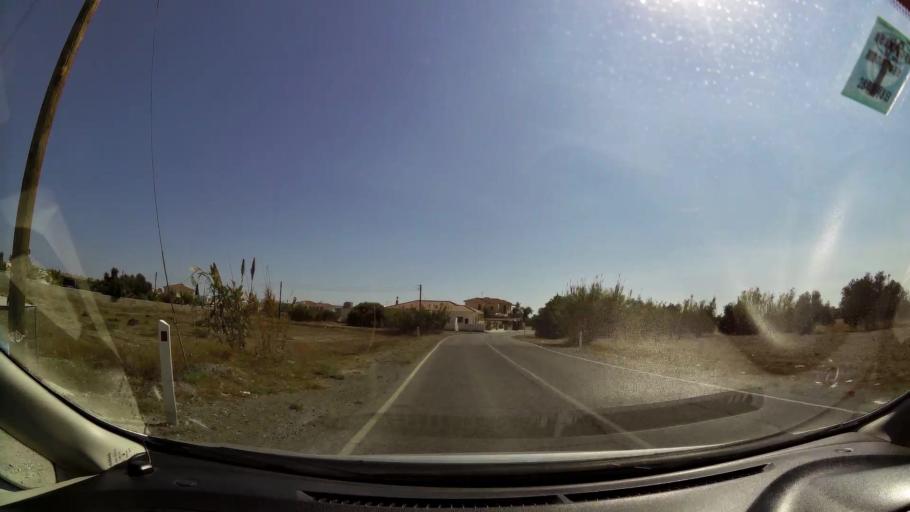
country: CY
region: Larnaka
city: Livadia
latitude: 34.9559
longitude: 33.6217
